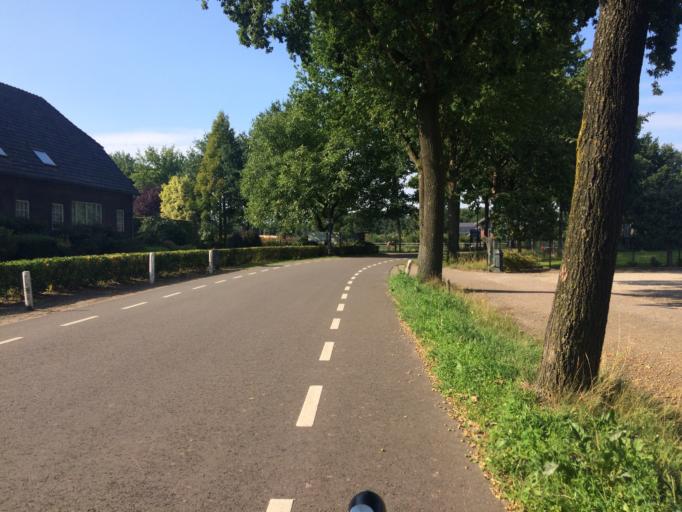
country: NL
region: North Brabant
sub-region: Gemeente Vught
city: Vught
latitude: 51.6635
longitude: 5.2329
